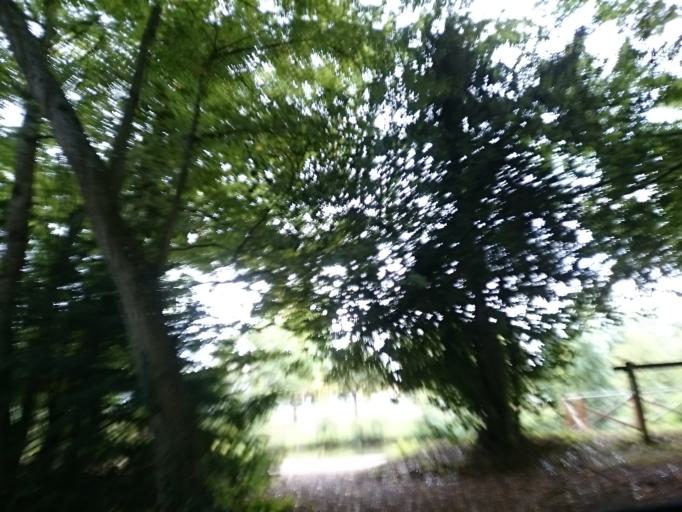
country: FR
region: Brittany
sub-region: Departement d'Ille-et-Vilaine
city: Cesson-Sevigne
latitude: 48.1171
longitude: -1.6013
